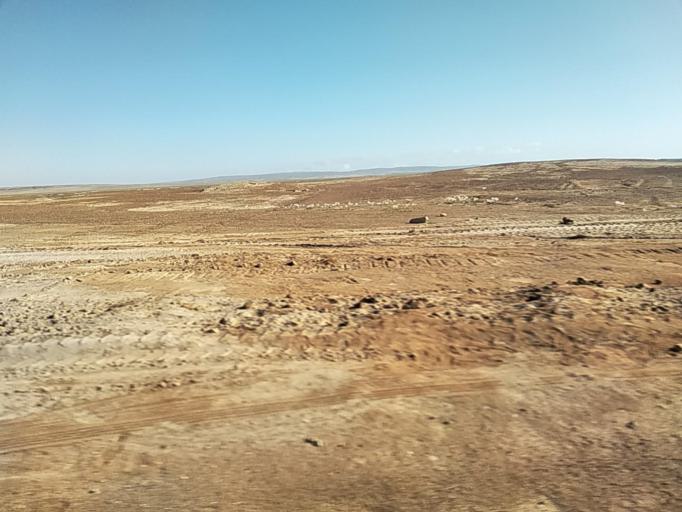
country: CL
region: Atacama
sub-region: Provincia de Copiapo
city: Copiapo
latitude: -27.3172
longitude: -70.8340
